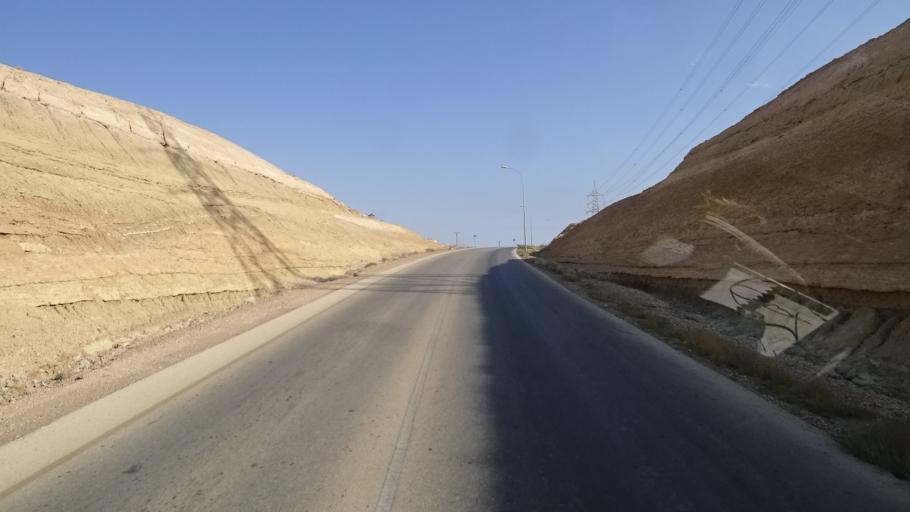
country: OM
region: Ash Sharqiyah
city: Sur
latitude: 22.5862
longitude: 59.4557
